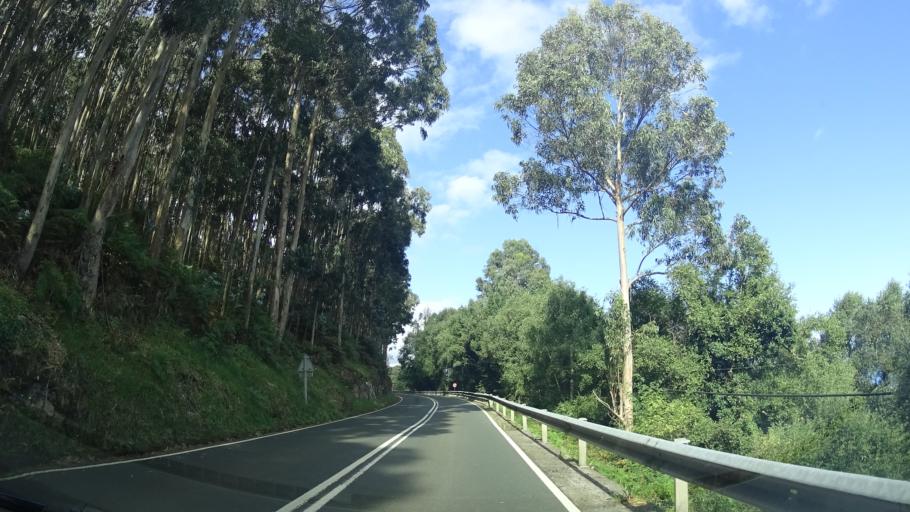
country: ES
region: Asturias
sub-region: Province of Asturias
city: Ribadesella
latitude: 43.4728
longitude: -5.1352
